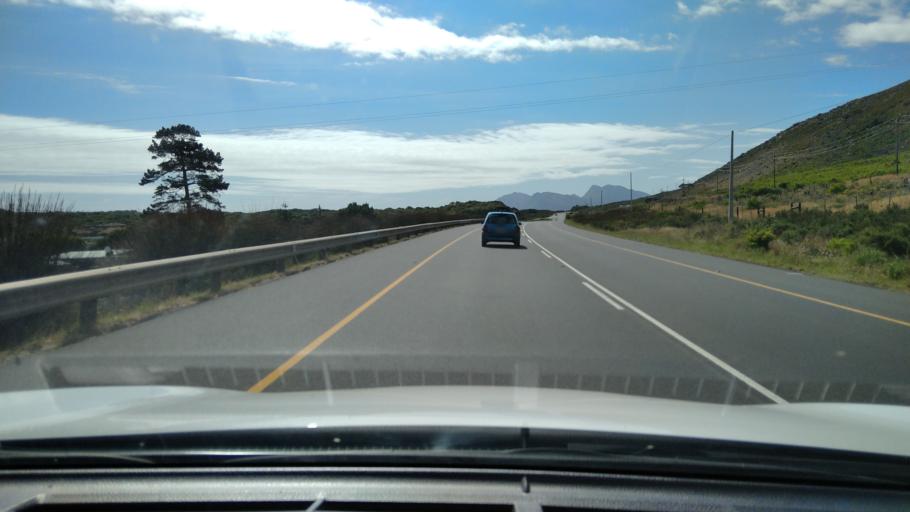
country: ZA
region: Western Cape
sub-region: Overberg District Municipality
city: Hermanus
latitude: -34.4076
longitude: 19.1530
